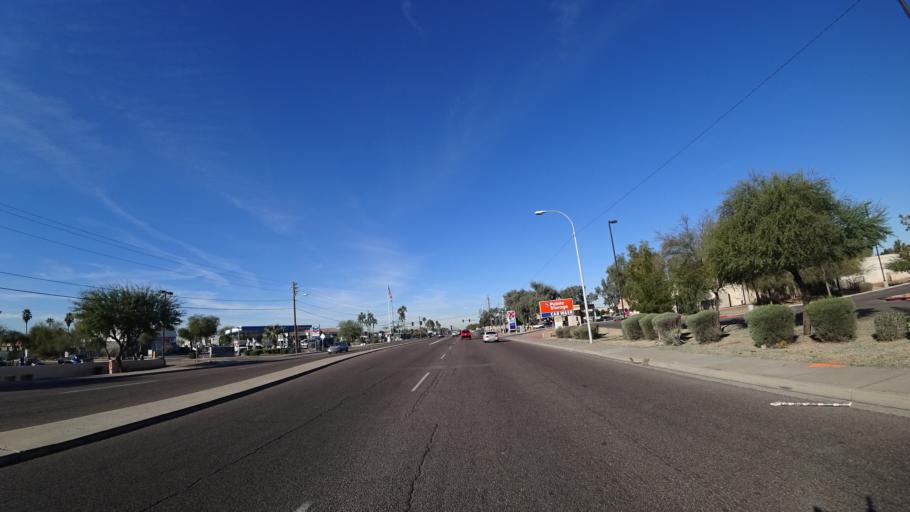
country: US
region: Arizona
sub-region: Maricopa County
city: Tolleson
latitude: 33.4658
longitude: -112.2188
